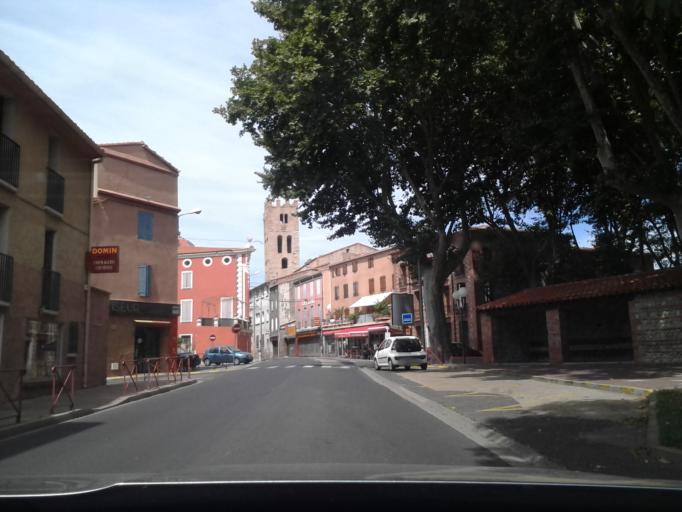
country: FR
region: Languedoc-Roussillon
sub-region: Departement des Pyrenees-Orientales
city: Millas
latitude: 42.6916
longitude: 2.6981
